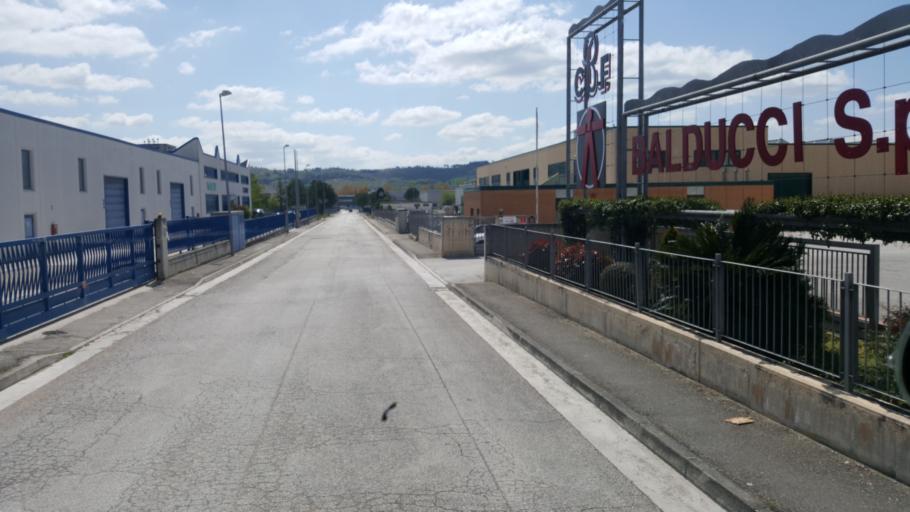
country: IT
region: The Marches
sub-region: Provincia di Macerata
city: Montecassiano
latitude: 43.3561
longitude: 13.4567
